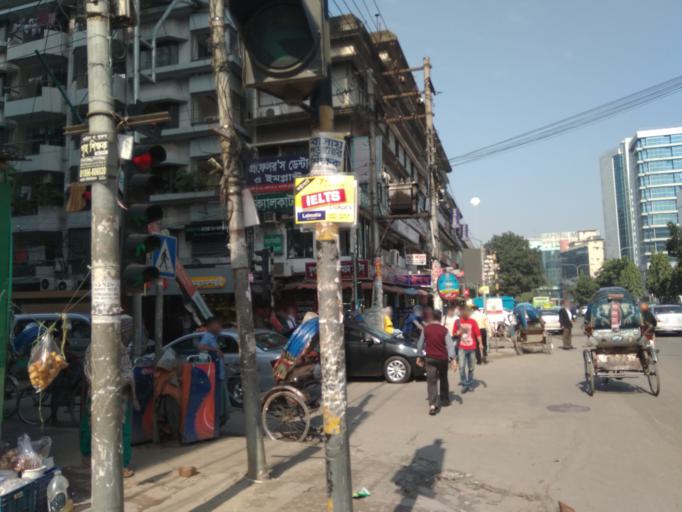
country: BD
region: Dhaka
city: Azimpur
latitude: 23.7436
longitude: 90.3822
